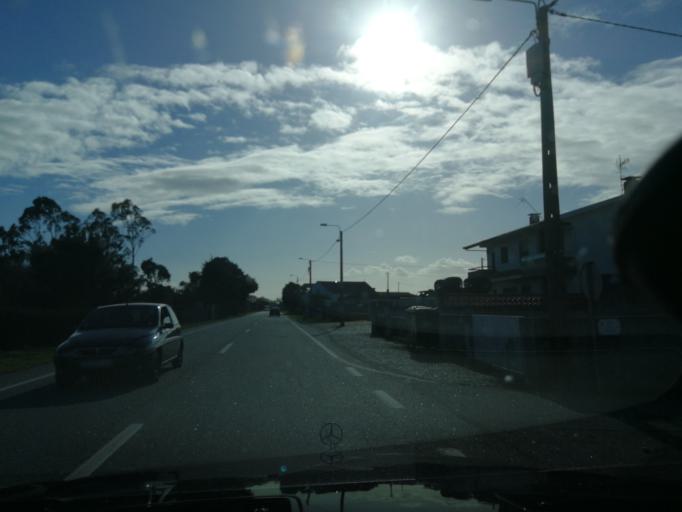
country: PT
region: Aveiro
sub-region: Estarreja
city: Pardilho
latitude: 40.8248
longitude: -8.6671
